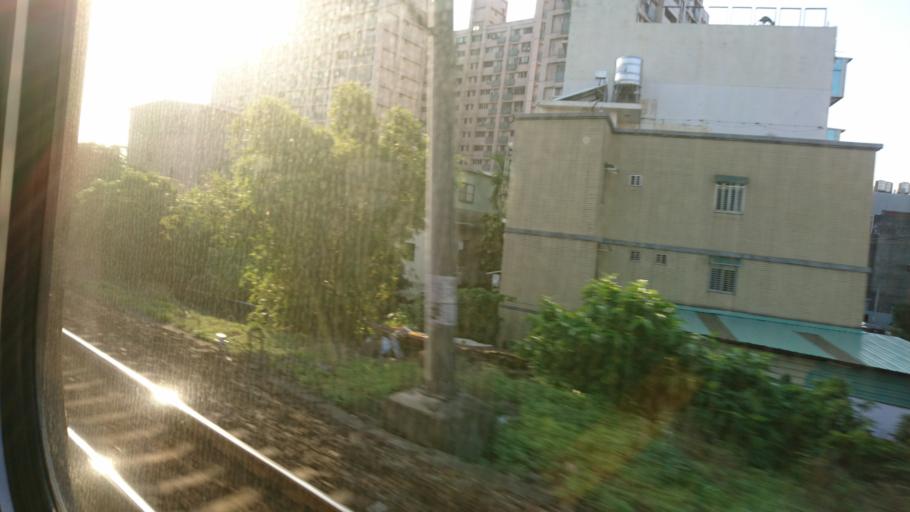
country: TW
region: Taiwan
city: Taoyuan City
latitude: 24.9456
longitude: 121.2167
